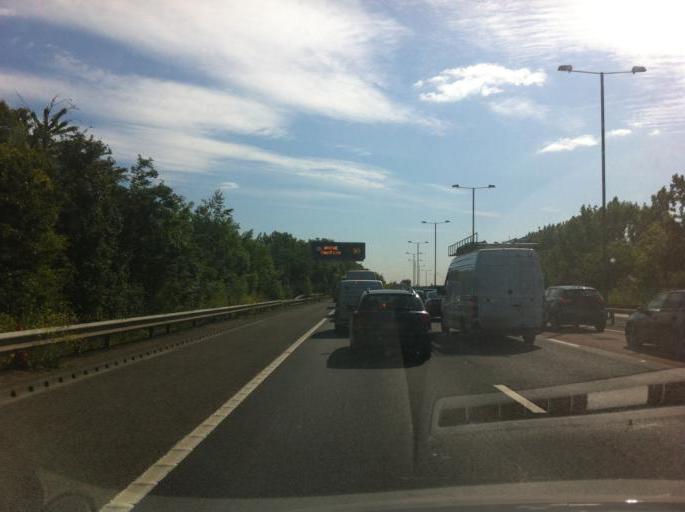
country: GB
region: England
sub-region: Greater London
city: Isleworth
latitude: 51.4959
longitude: -0.3394
